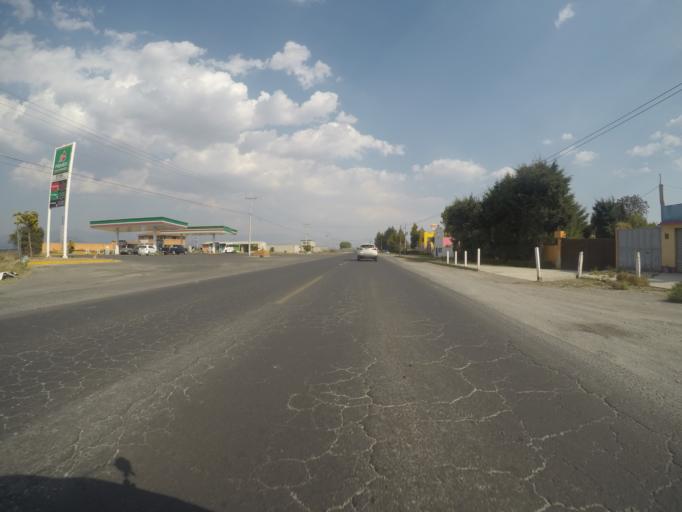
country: MX
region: Morelos
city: Chapultepec
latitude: 19.1936
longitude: -99.5385
